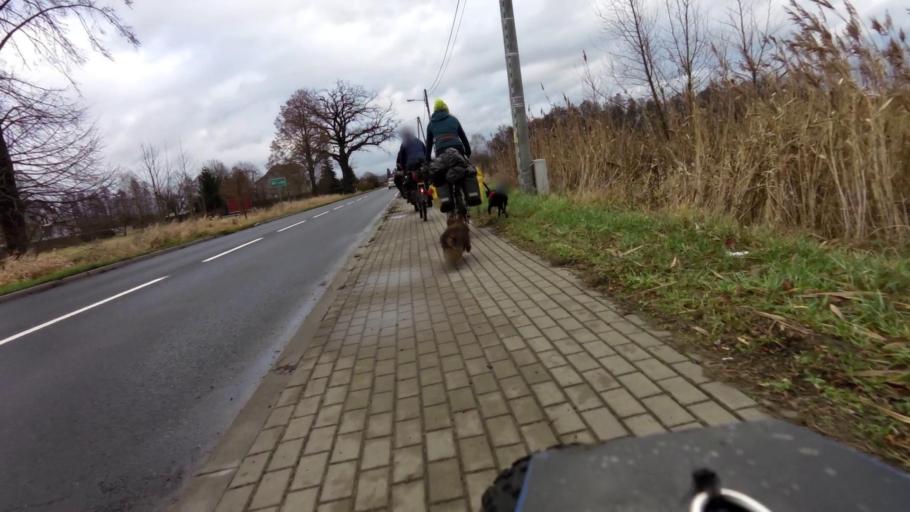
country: PL
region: Lubusz
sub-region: Powiat gorzowski
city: Witnica
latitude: 52.6746
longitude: 14.9117
